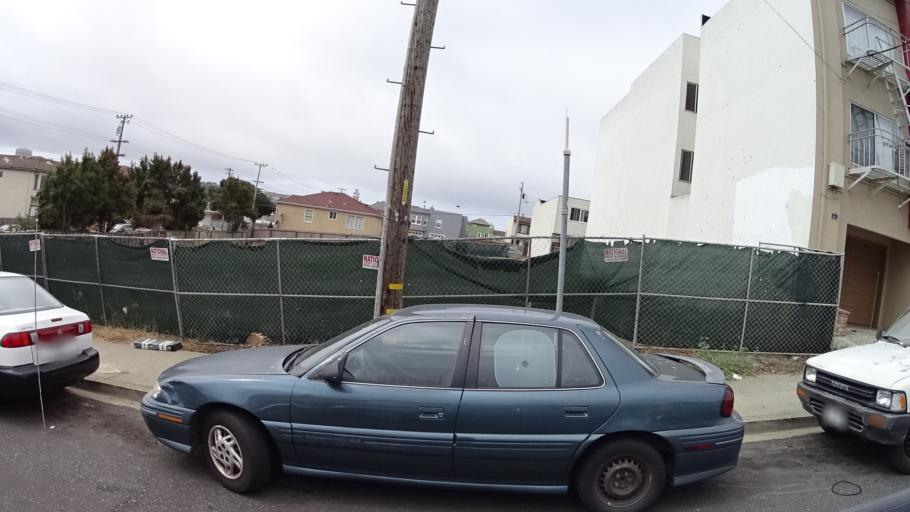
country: US
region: California
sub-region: San Mateo County
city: Daly City
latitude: 37.6921
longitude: -122.4626
